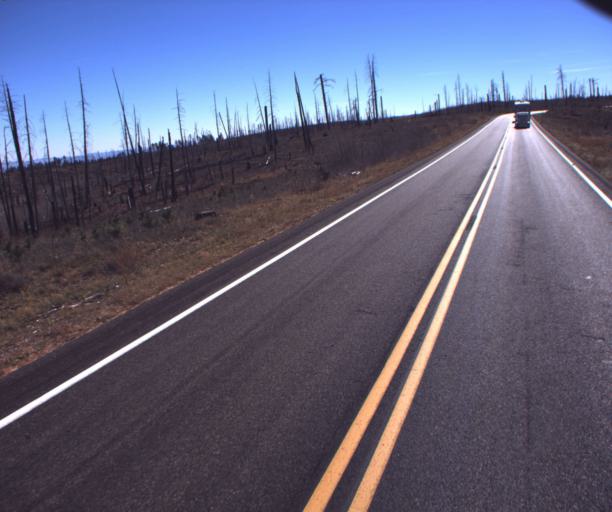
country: US
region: Arizona
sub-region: Coconino County
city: Fredonia
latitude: 36.6226
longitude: -112.1781
